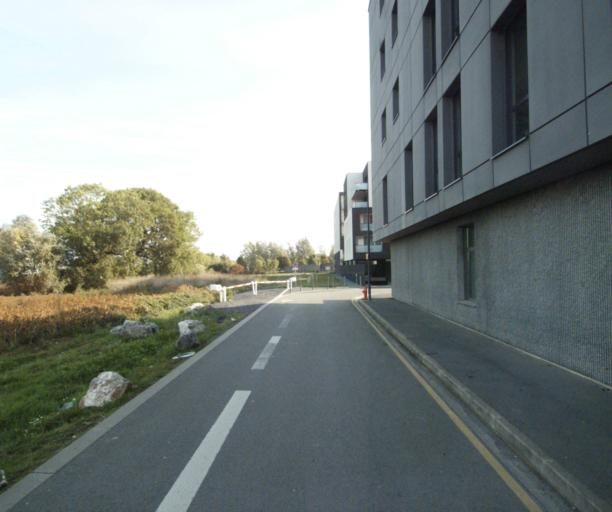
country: FR
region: Nord-Pas-de-Calais
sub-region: Departement du Nord
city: Capinghem
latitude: 50.6529
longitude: 2.9723
